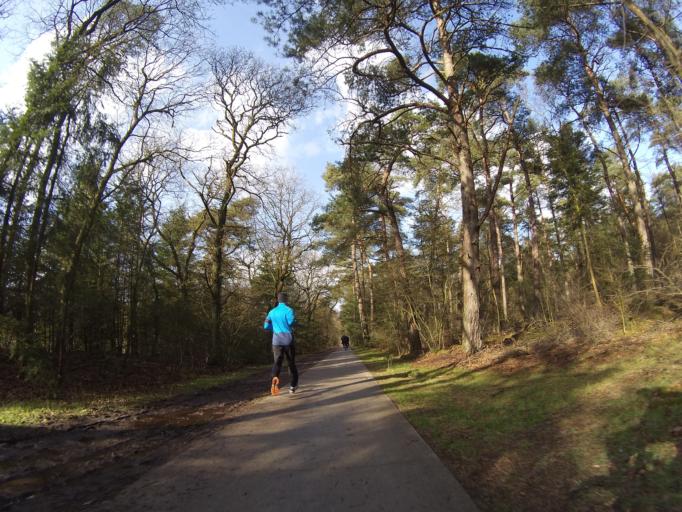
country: NL
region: Utrecht
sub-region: Gemeente Soest
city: Soest
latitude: 52.1513
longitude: 5.2540
